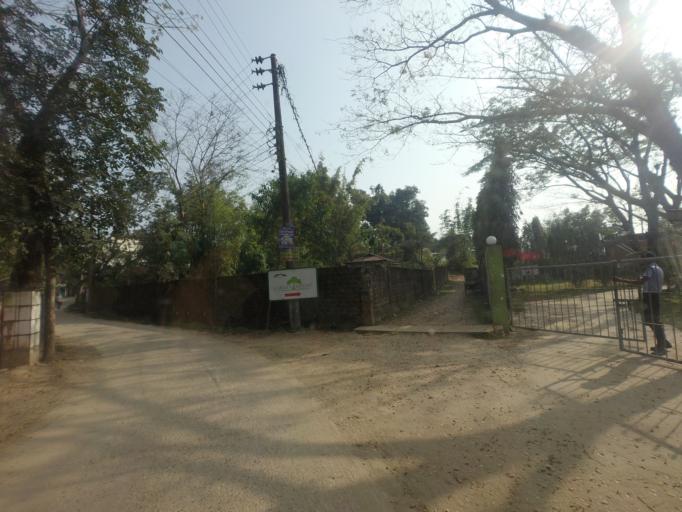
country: BD
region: Sylhet
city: Sylhet
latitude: 24.9105
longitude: 91.9415
